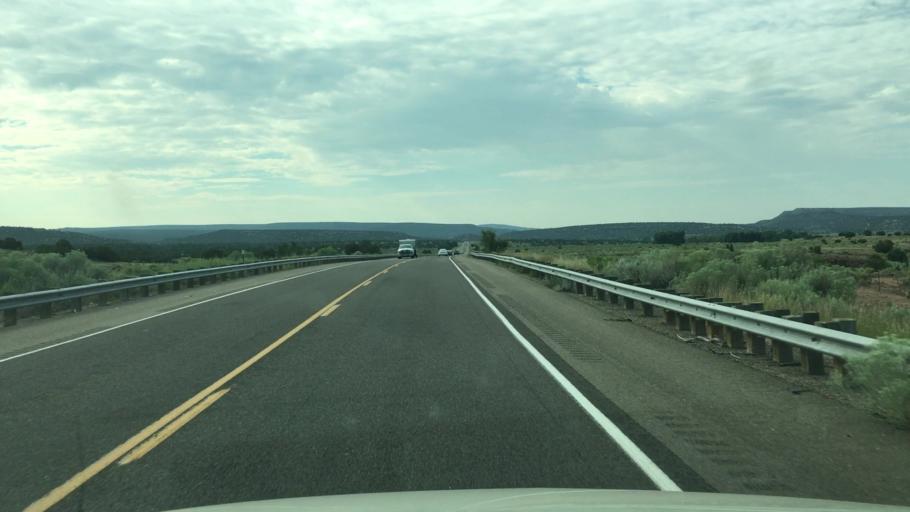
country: US
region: New Mexico
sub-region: Santa Fe County
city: Eldorado at Santa Fe
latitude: 35.4127
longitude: -105.8676
